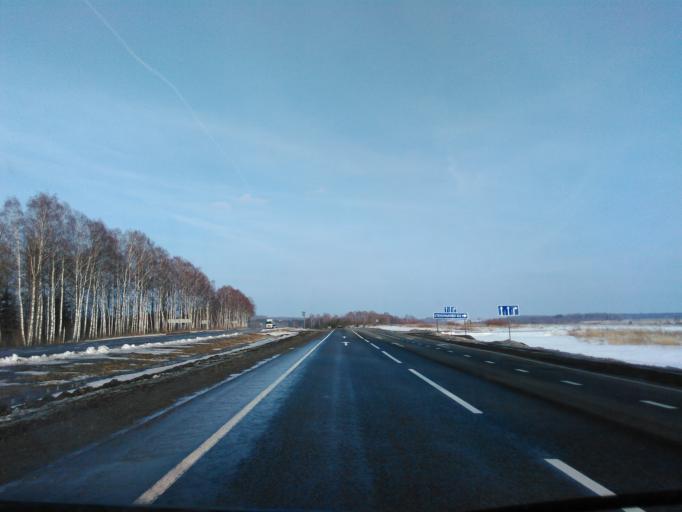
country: RU
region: Smolensk
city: Vyaz'ma
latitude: 55.2027
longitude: 34.1384
